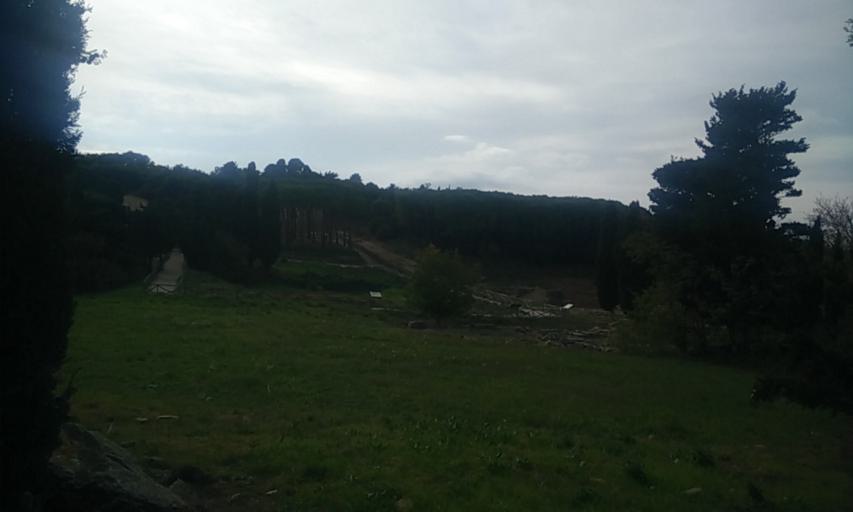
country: IT
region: Tuscany
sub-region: Provincia di Livorno
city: Piombino
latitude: 42.9888
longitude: 10.4905
